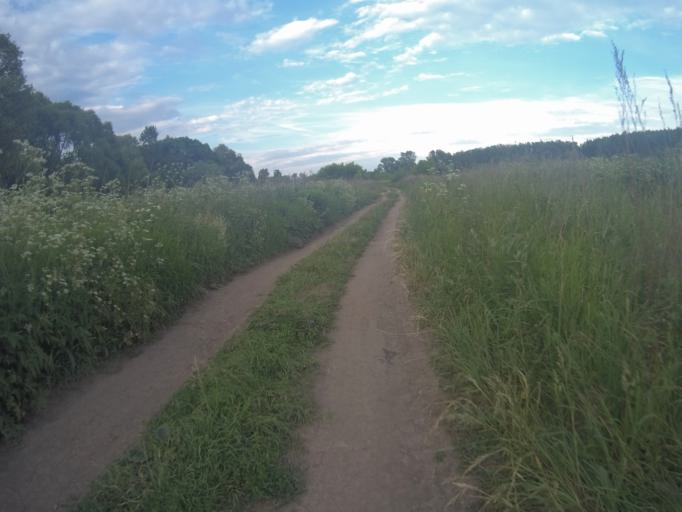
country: RU
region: Vladimir
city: Vladimir
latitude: 56.1939
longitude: 40.3798
